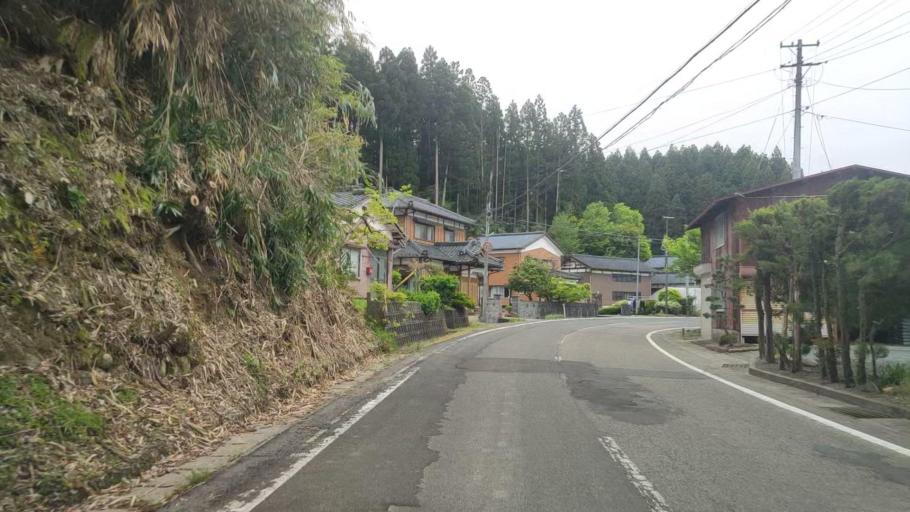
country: JP
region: Niigata
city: Gosen
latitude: 37.7250
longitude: 139.1356
